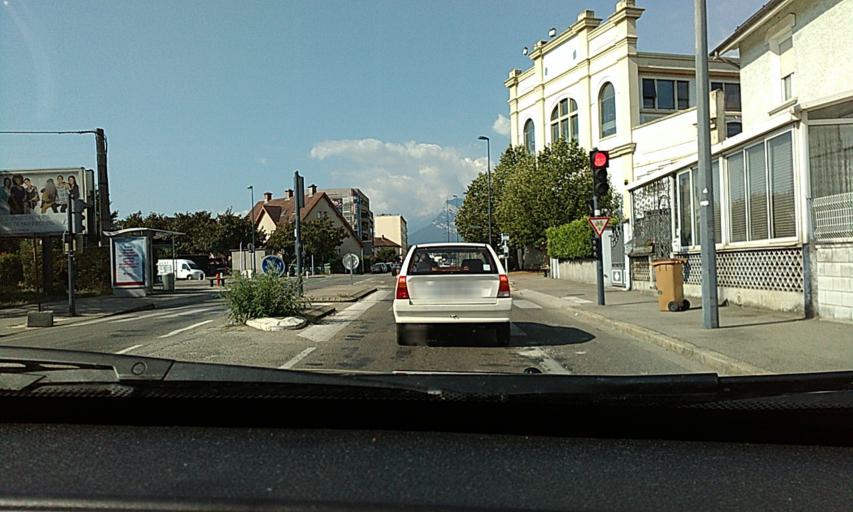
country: FR
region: Rhone-Alpes
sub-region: Departement de l'Isere
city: Grenoble
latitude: 45.1644
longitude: 5.7180
